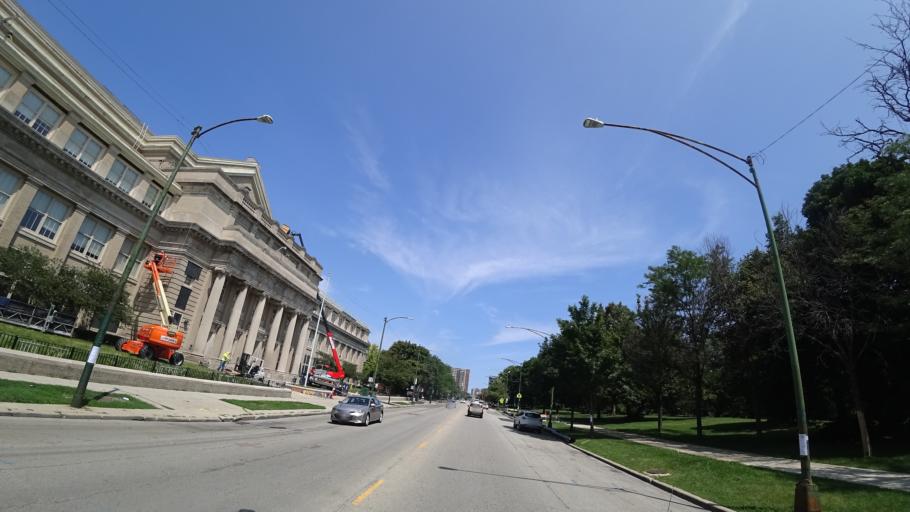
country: US
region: Illinois
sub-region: Cook County
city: Chicago
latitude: 41.7820
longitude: -87.5865
